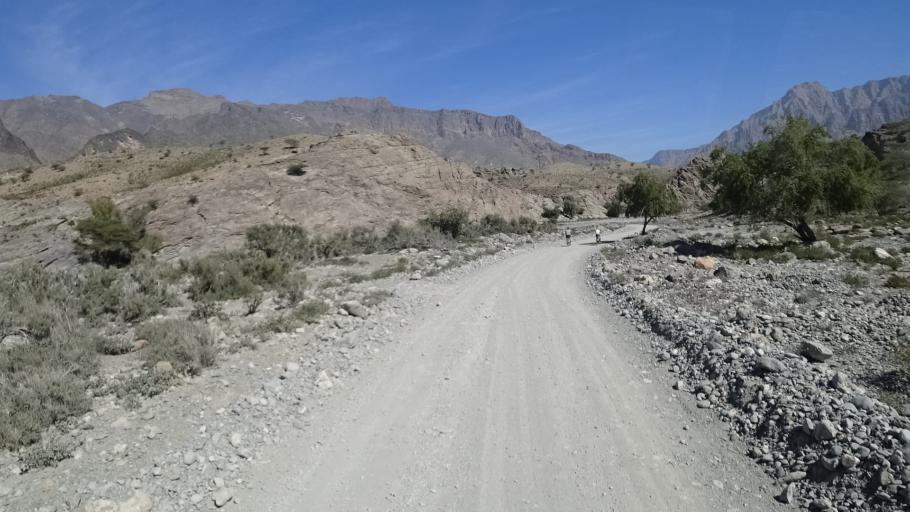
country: OM
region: Al Batinah
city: Bayt al `Awabi
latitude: 23.2585
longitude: 57.4312
